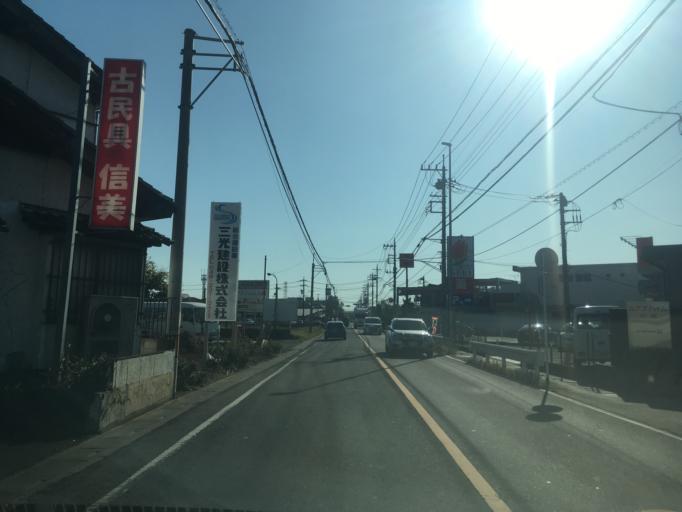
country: JP
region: Saitama
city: Kawagoe
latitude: 35.8854
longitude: 139.4767
